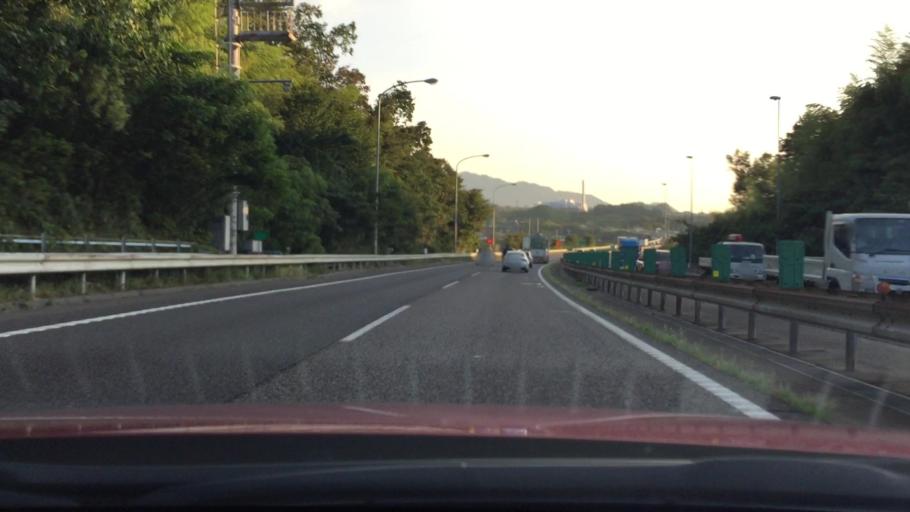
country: JP
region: Shiga Prefecture
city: Moriyama
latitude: 35.0307
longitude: 136.0432
